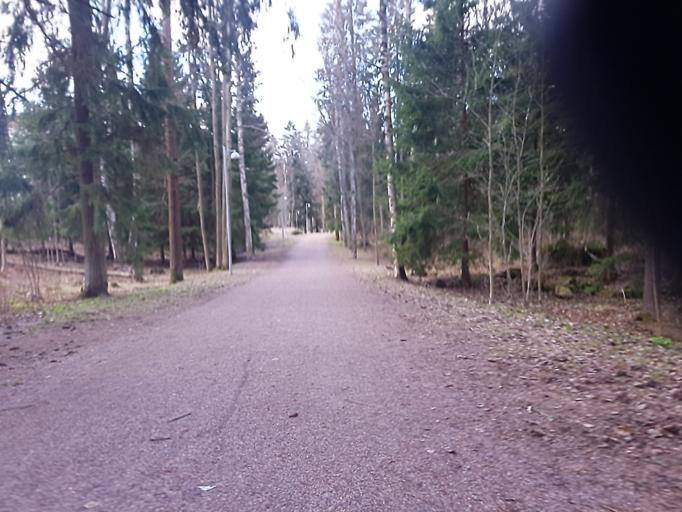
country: FI
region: Uusimaa
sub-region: Helsinki
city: Teekkarikylae
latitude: 60.2284
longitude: 24.8866
